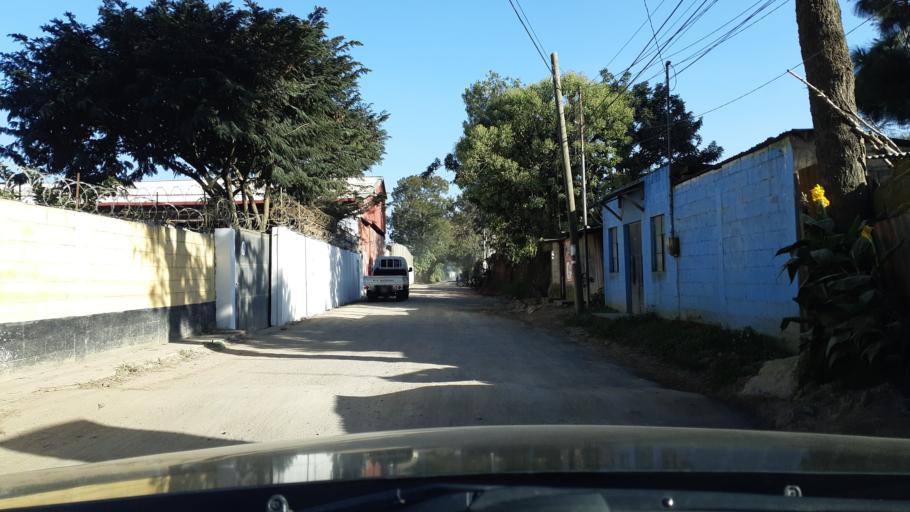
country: GT
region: Chimaltenango
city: El Tejar
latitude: 14.6395
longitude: -90.8058
